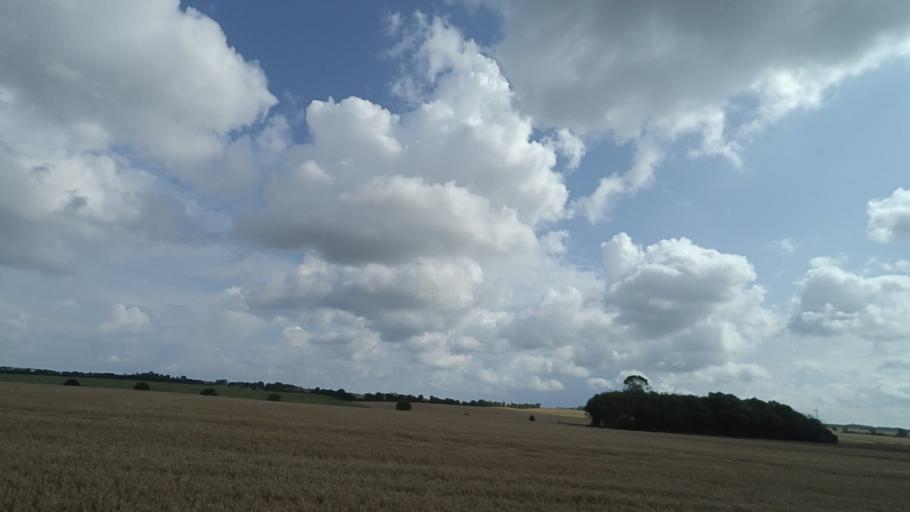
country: DK
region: Central Jutland
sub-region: Norddjurs Kommune
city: Auning
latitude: 56.4948
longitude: 10.4423
